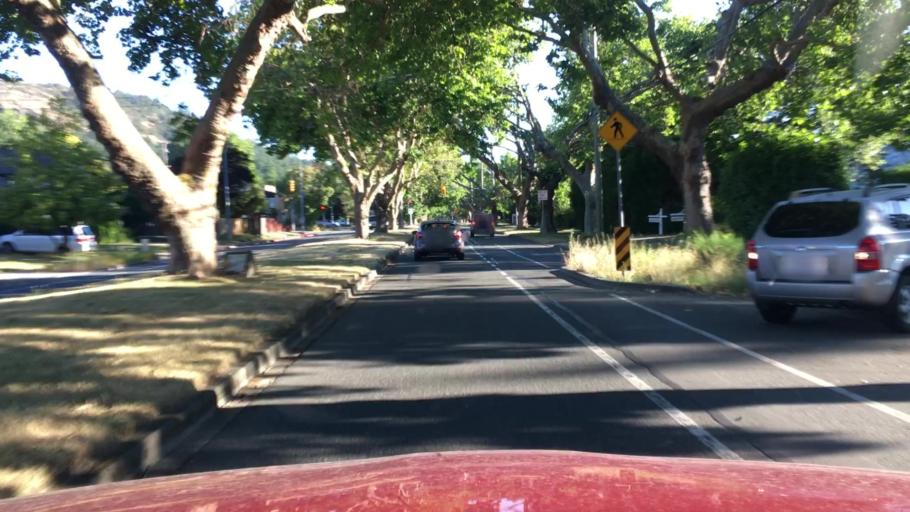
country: CA
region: British Columbia
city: Oak Bay
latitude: 48.4830
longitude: -123.3367
